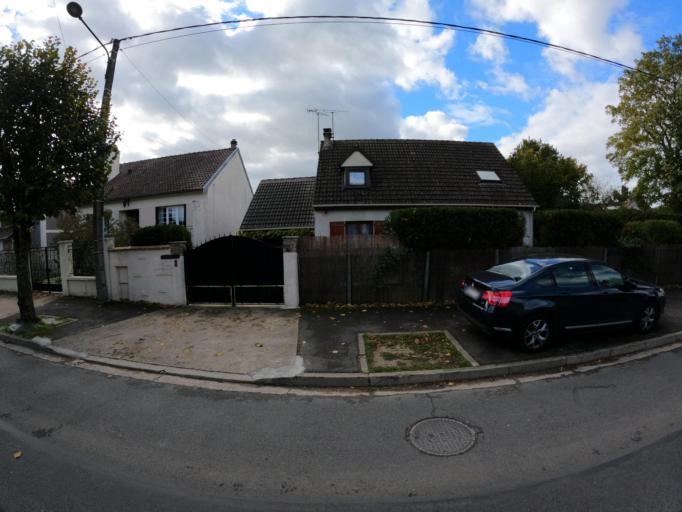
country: FR
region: Ile-de-France
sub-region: Departement de Seine-et-Marne
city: Montry
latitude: 48.8867
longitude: 2.8327
